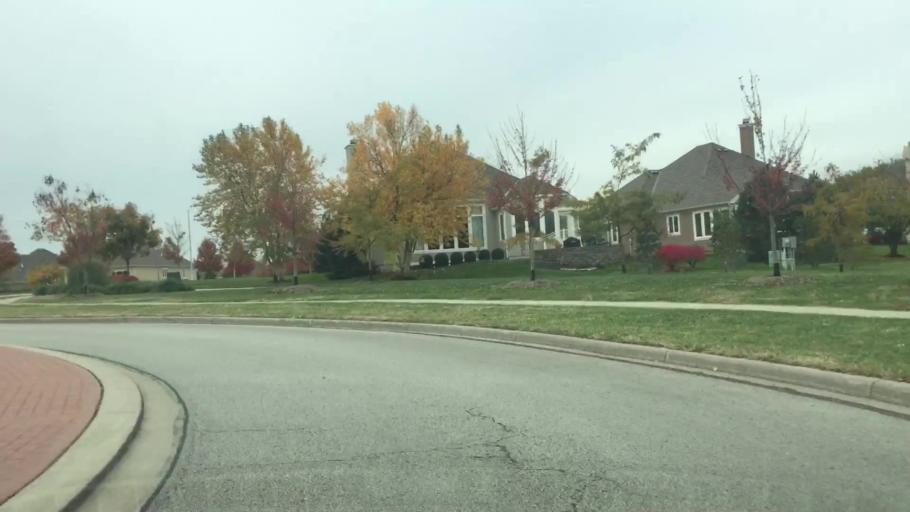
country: US
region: Kansas
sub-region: Johnson County
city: Lenexa
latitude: 38.9193
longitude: -94.7501
